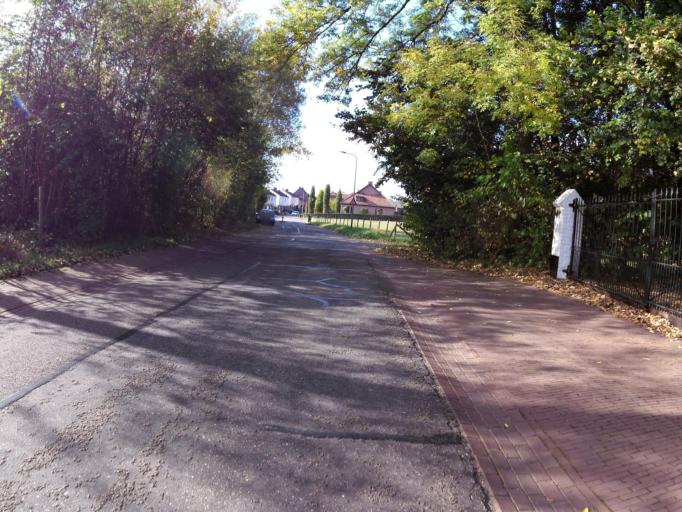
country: NL
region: Limburg
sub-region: Gemeente Schinnen
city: Schinnen
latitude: 50.9455
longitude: 5.8864
